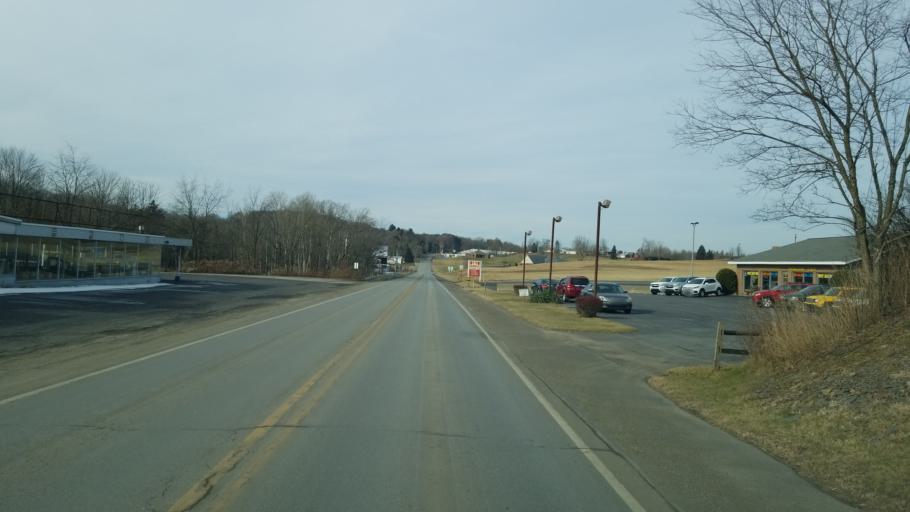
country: US
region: Pennsylvania
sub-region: Jefferson County
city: Punxsutawney
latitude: 40.9567
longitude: -79.0009
